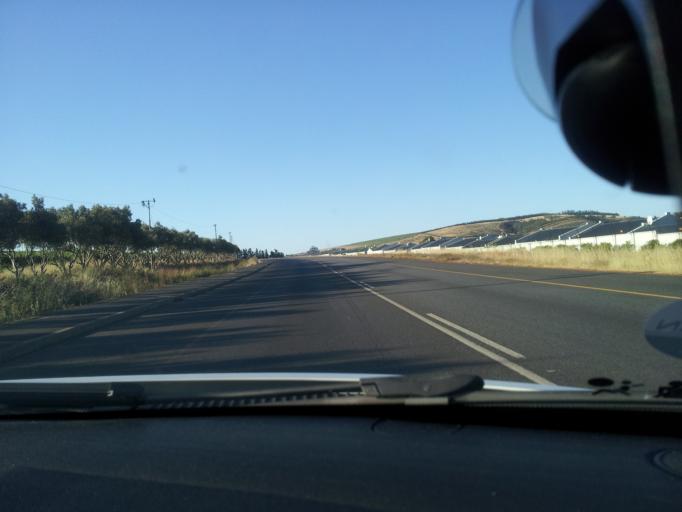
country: ZA
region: Western Cape
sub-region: Cape Winelands District Municipality
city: Stellenbosch
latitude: -33.9108
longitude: 18.8476
